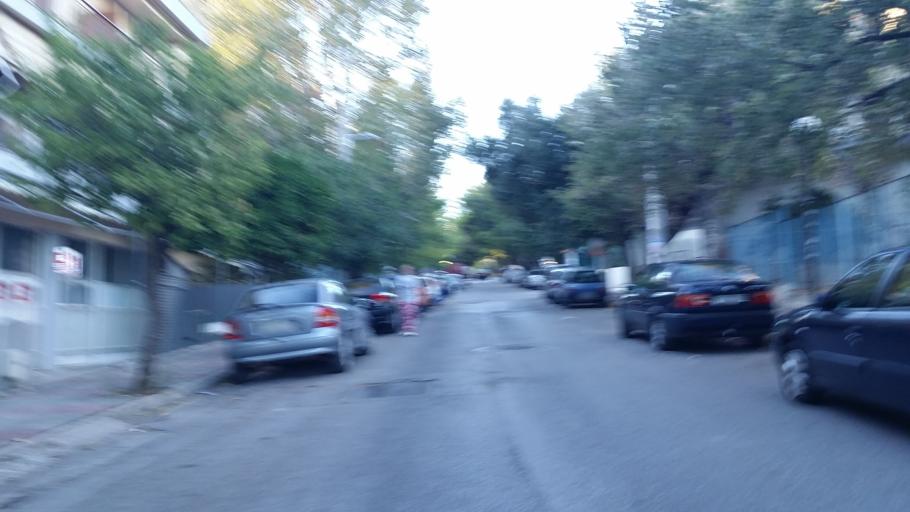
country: GR
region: Attica
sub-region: Nomarchia Athinas
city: Irakleio
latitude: 38.0486
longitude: 23.7595
